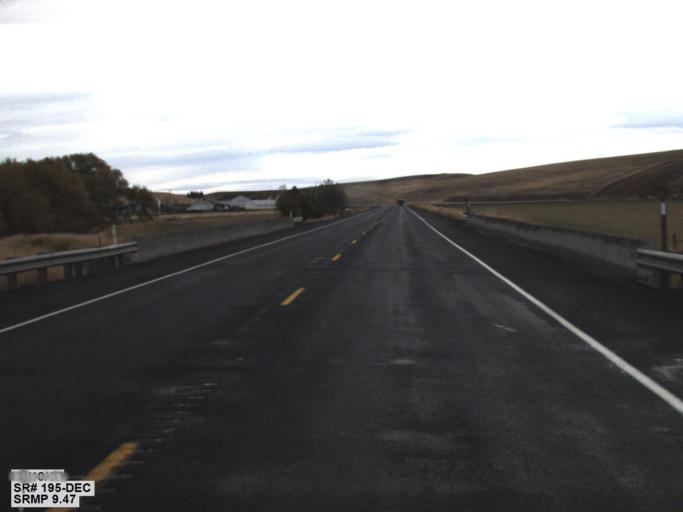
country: US
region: Washington
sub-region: Whitman County
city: Pullman
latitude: 46.5765
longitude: -117.1499
